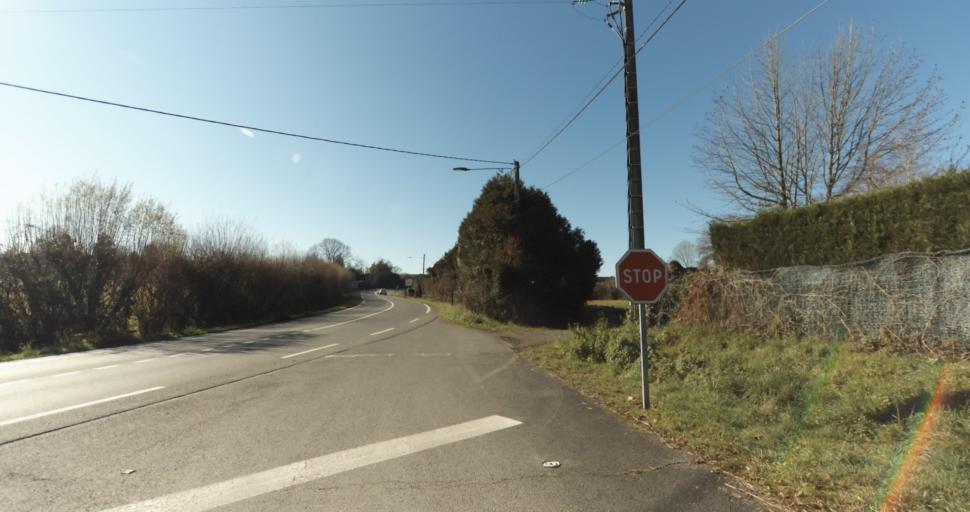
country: FR
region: Aquitaine
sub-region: Departement des Pyrenees-Atlantiques
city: Morlaas
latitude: 43.3376
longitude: -0.2732
